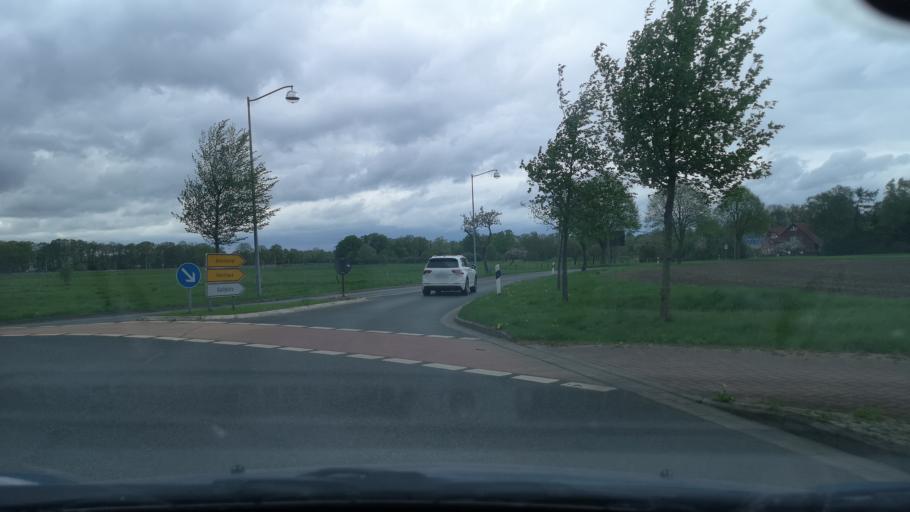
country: DE
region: Lower Saxony
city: Langenhagen
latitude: 52.4856
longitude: 9.7395
